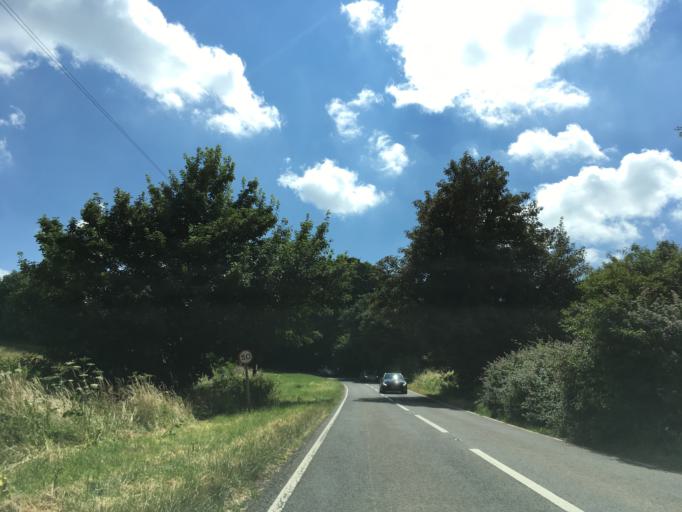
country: GB
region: England
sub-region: Gloucestershire
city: Painswick
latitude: 51.8135
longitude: -2.2044
